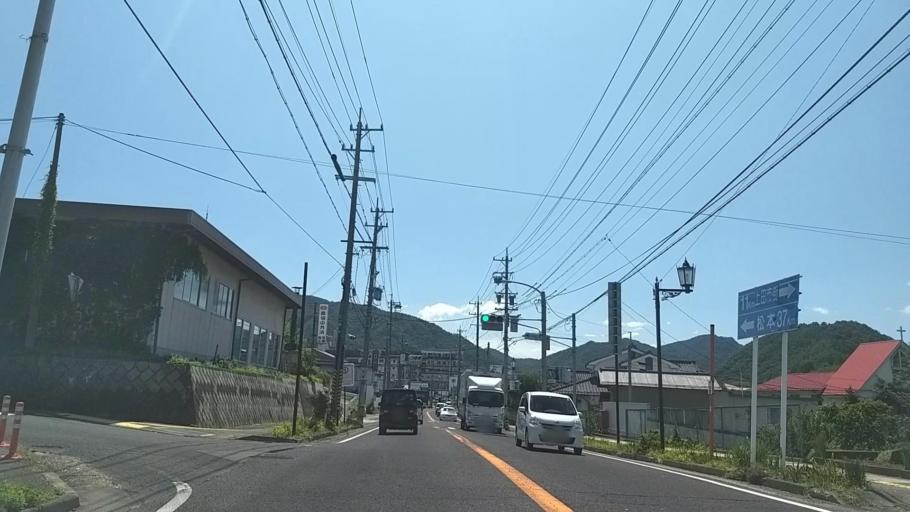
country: JP
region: Nagano
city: Kamimaruko
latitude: 36.3296
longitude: 138.2699
